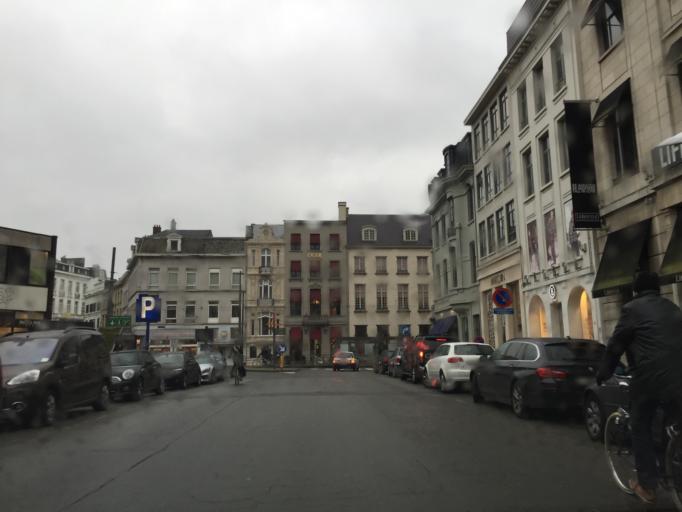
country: BE
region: Flanders
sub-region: Provincie Antwerpen
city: Antwerpen
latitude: 51.2160
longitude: 4.4041
